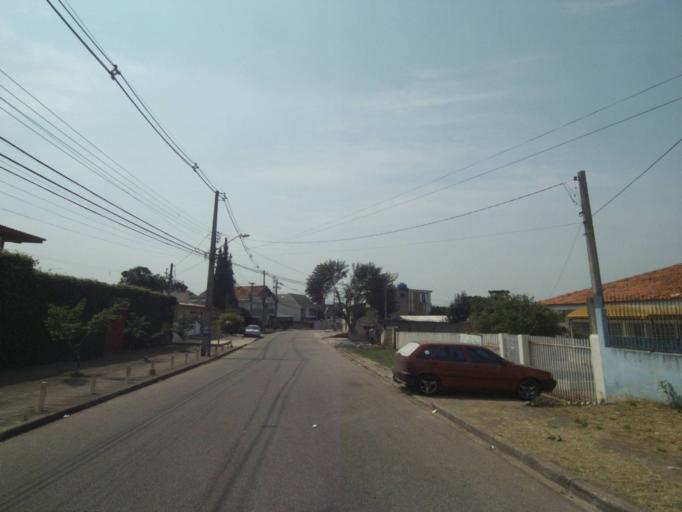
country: BR
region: Parana
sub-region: Pinhais
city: Pinhais
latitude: -25.4852
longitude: -49.2099
